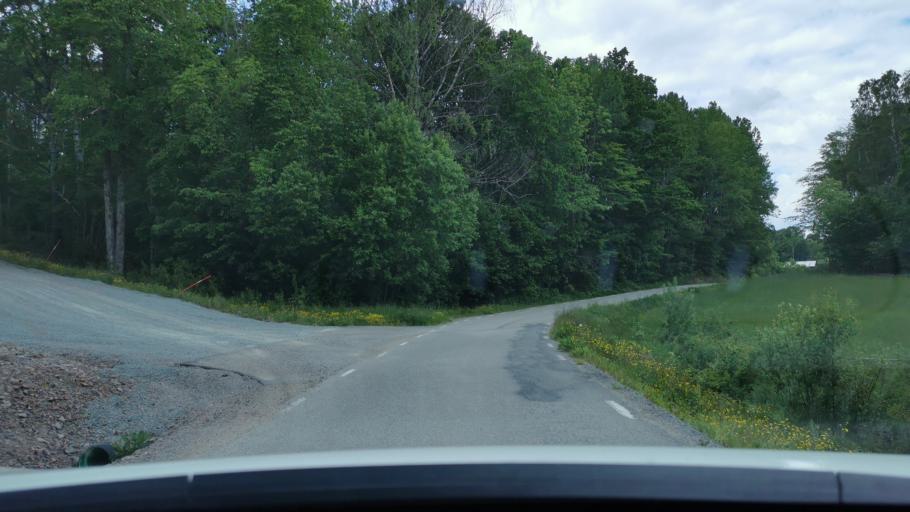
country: SE
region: Vaestra Goetaland
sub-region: Bengtsfors Kommun
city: Dals Langed
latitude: 58.8374
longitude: 12.3300
